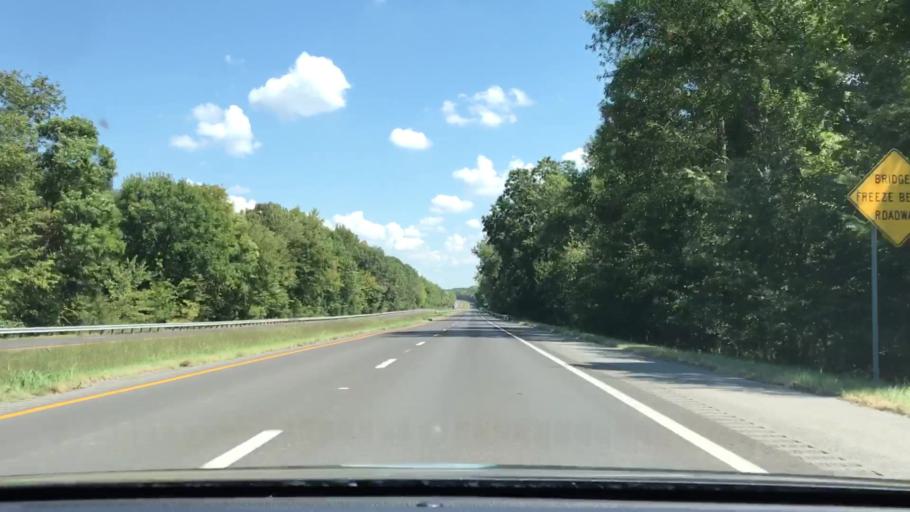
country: US
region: Kentucky
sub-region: Fulton County
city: Fulton
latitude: 36.5934
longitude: -88.8103
